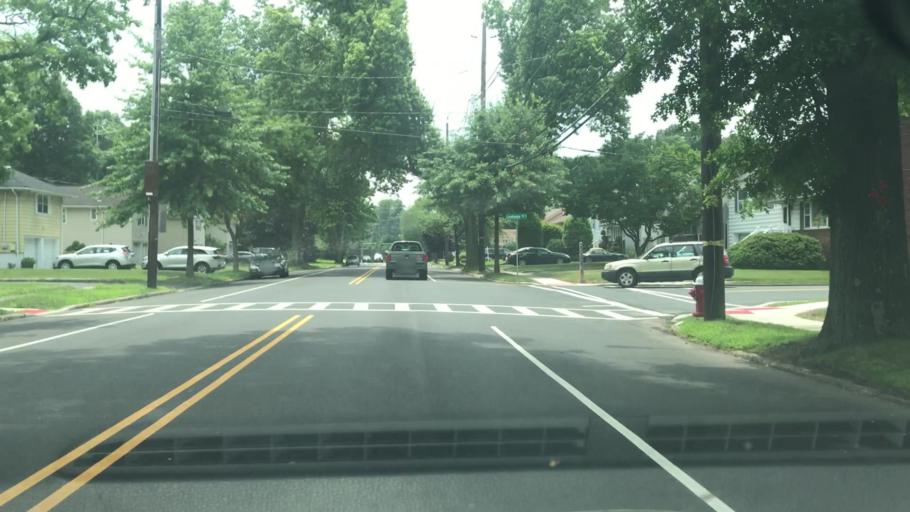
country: US
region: New Jersey
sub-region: Union County
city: Clark
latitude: 40.6435
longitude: -74.3051
